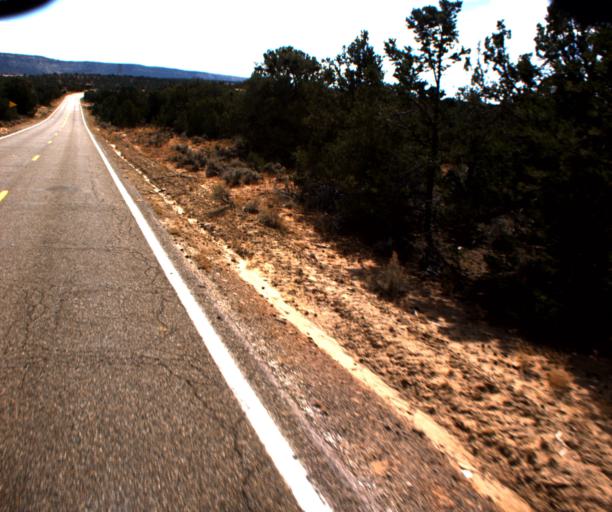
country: US
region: Arizona
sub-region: Navajo County
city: Kayenta
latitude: 36.6166
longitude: -110.5039
